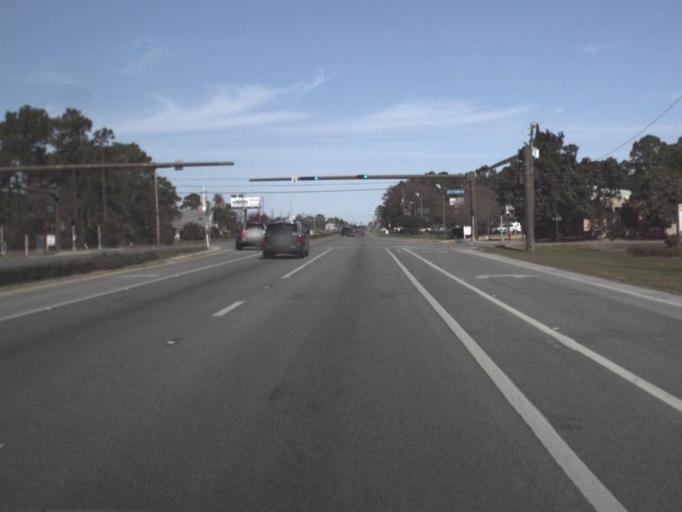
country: US
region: Florida
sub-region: Bay County
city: Hiland Park
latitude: 30.1961
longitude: -85.6497
